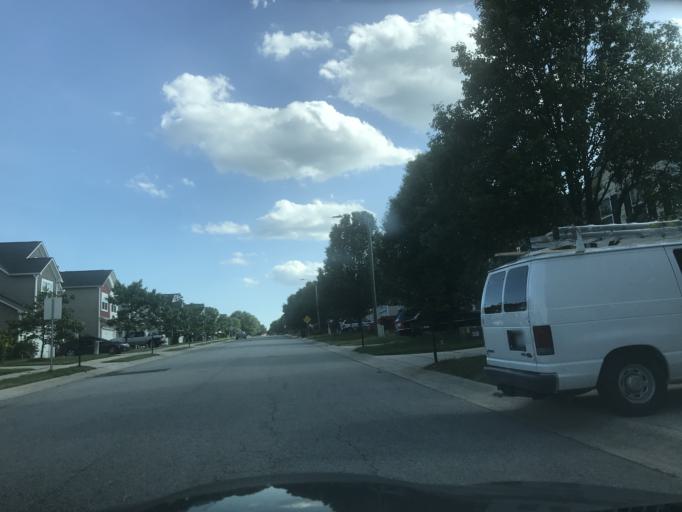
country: US
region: North Carolina
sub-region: Wake County
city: Knightdale
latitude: 35.8392
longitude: -78.5478
